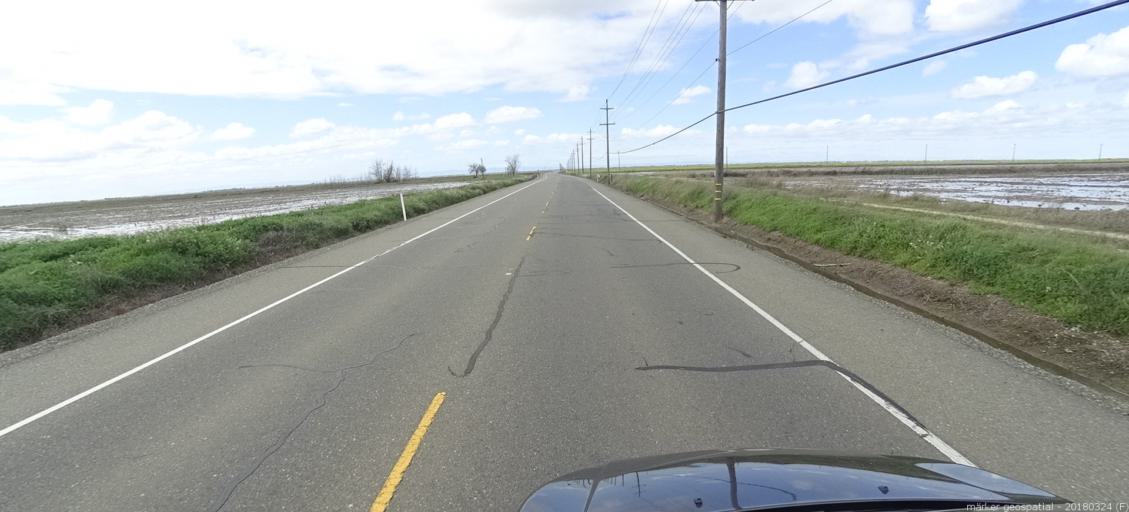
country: US
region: California
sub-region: Sacramento County
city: Elverta
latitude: 38.7145
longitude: -121.4995
